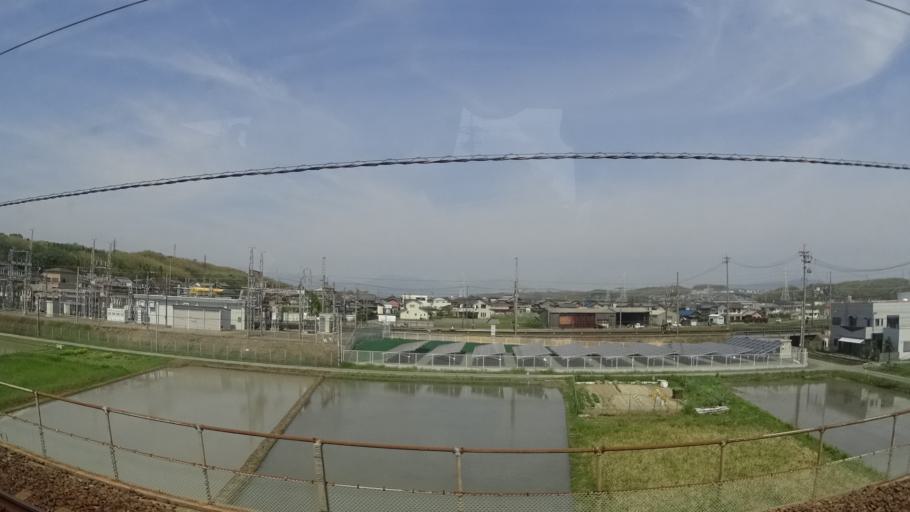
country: JP
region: Mie
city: Yokkaichi
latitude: 35.0491
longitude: 136.6714
